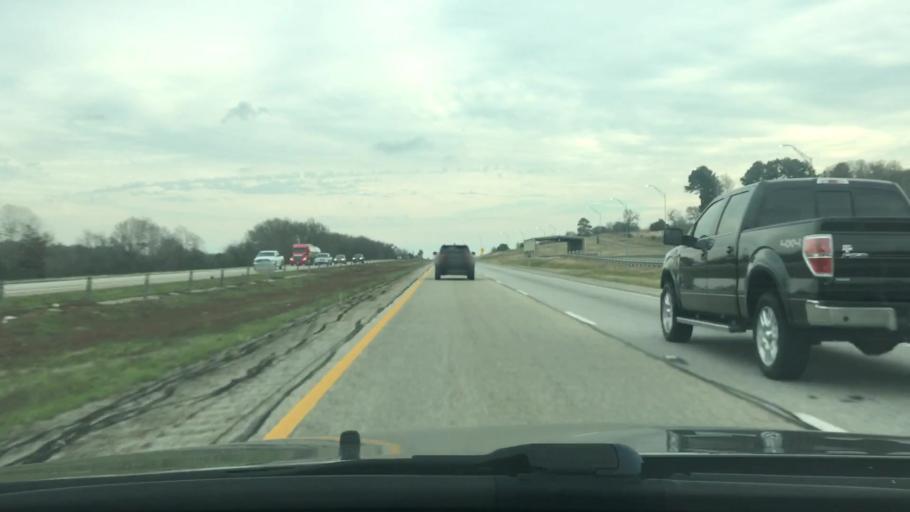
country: US
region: Texas
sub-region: Leon County
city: Centerville
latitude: 31.2807
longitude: -95.9913
